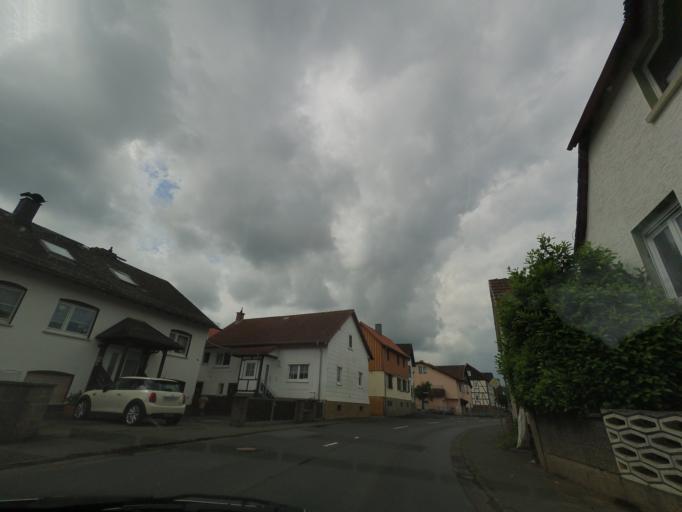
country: DE
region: Hesse
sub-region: Regierungsbezirk Giessen
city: Lohra
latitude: 50.6869
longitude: 8.6087
